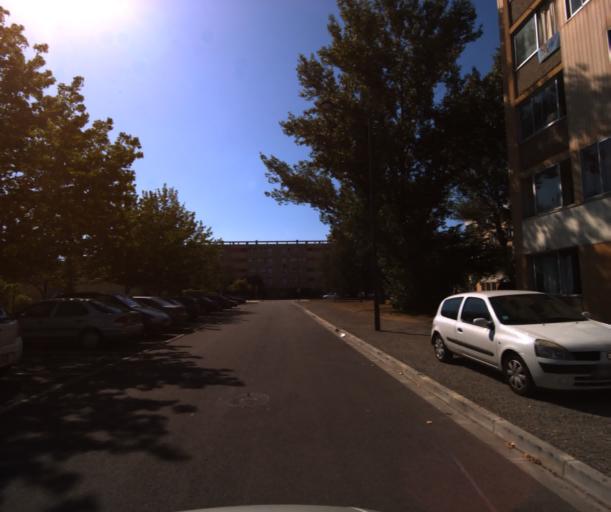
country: FR
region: Midi-Pyrenees
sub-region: Departement de la Haute-Garonne
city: Muret
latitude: 43.4688
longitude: 1.3335
